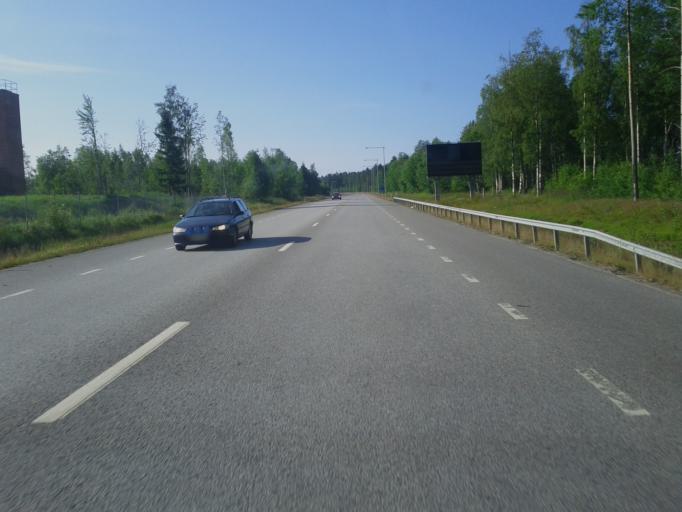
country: SE
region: Vaesterbotten
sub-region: Umea Kommun
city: Umea
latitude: 63.7879
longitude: 20.3015
